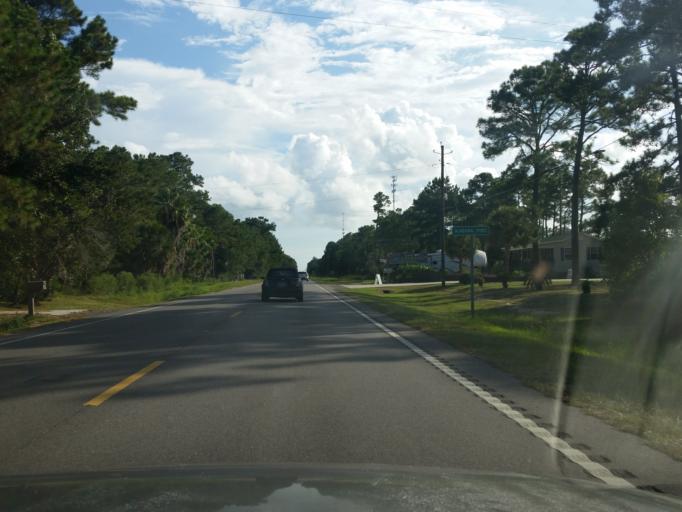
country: US
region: Alabama
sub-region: Mobile County
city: Dauphin Island
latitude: 30.3685
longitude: -88.1117
